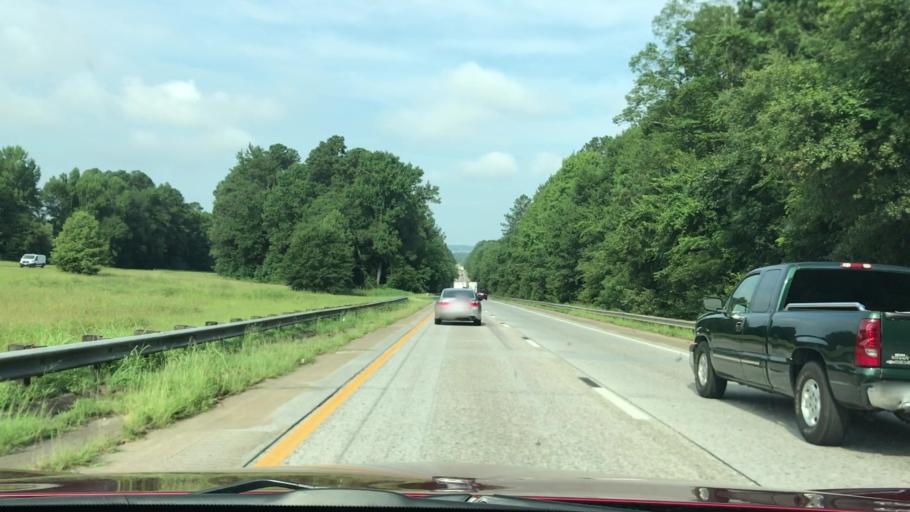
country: US
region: South Carolina
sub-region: Aiken County
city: Belvedere
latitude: 33.5458
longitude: -81.9694
